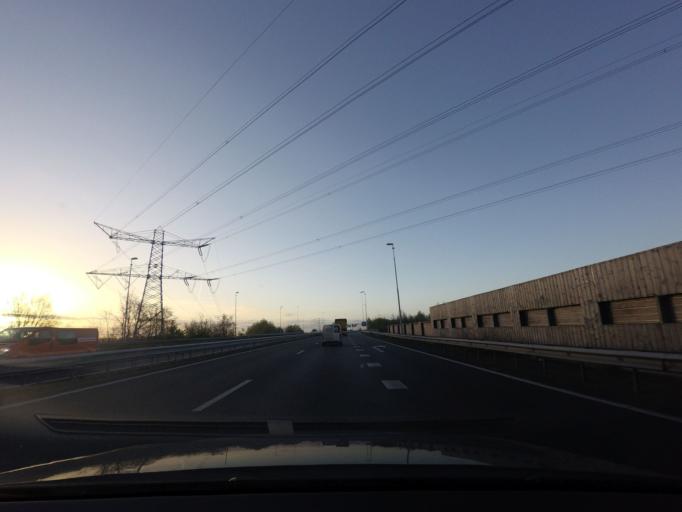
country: NL
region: North Holland
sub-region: Gemeente Zaanstad
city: Zaandam
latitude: 52.4586
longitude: 4.8364
